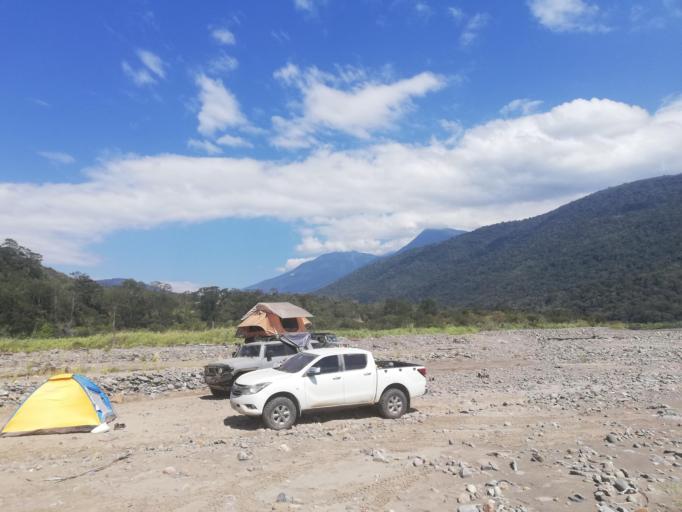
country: BO
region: La Paz
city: Quime
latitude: -16.4742
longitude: -66.7881
